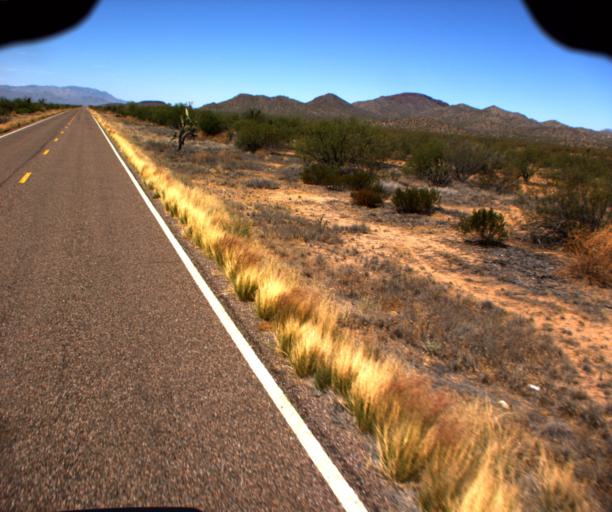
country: US
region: Arizona
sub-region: Yavapai County
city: Congress
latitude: 34.0489
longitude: -113.0604
